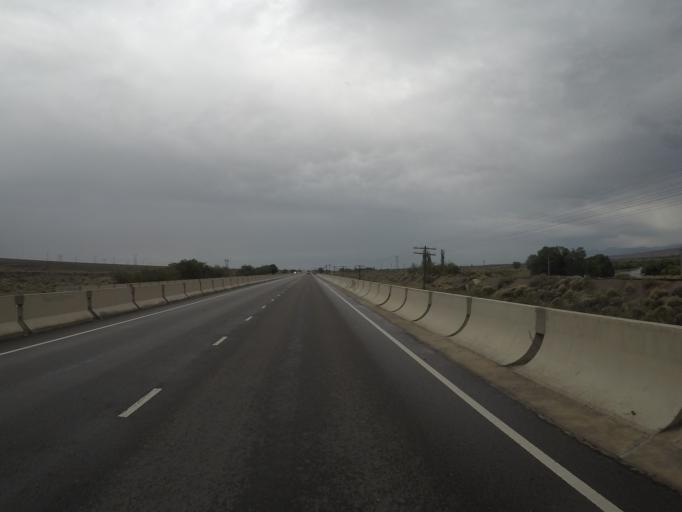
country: KG
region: Ysyk-Koel
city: Balykchy
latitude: 42.4603
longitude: 76.0744
